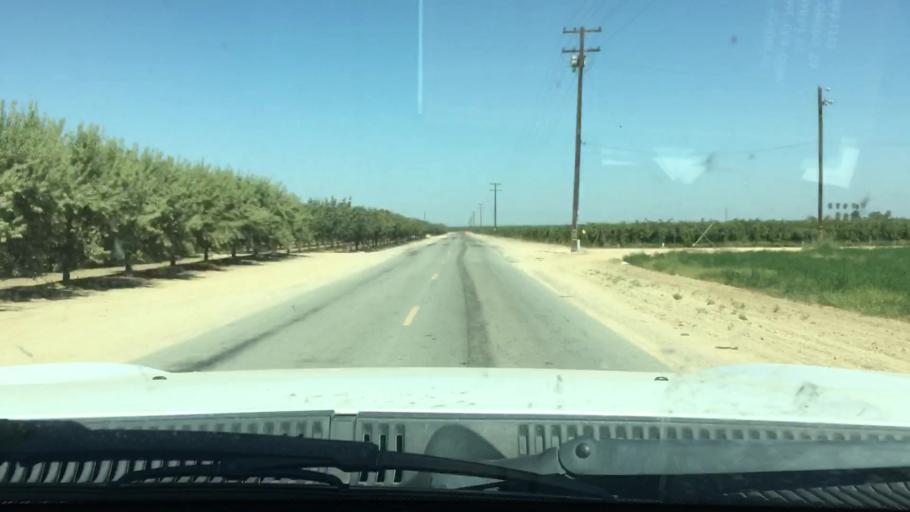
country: US
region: California
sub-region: Kern County
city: Shafter
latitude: 35.4324
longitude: -119.2874
